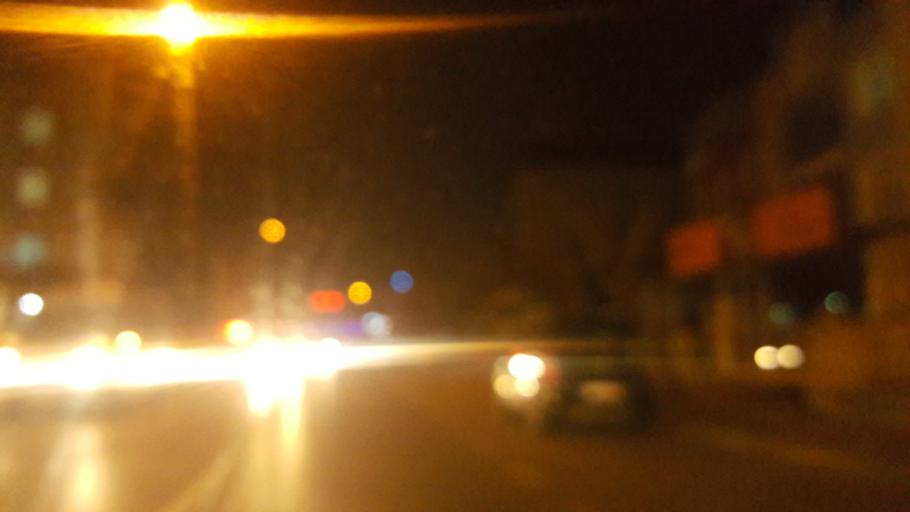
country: TR
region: Kocaeli
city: Darica
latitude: 40.7816
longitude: 29.3947
